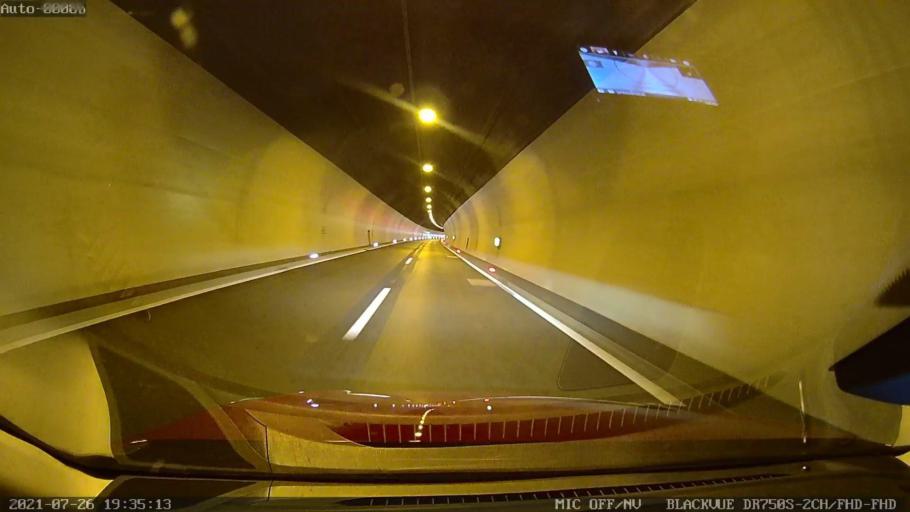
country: AT
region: Upper Austria
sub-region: Politischer Bezirk Kirchdorf an der Krems
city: Rossleithen
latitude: 47.7530
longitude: 14.2367
